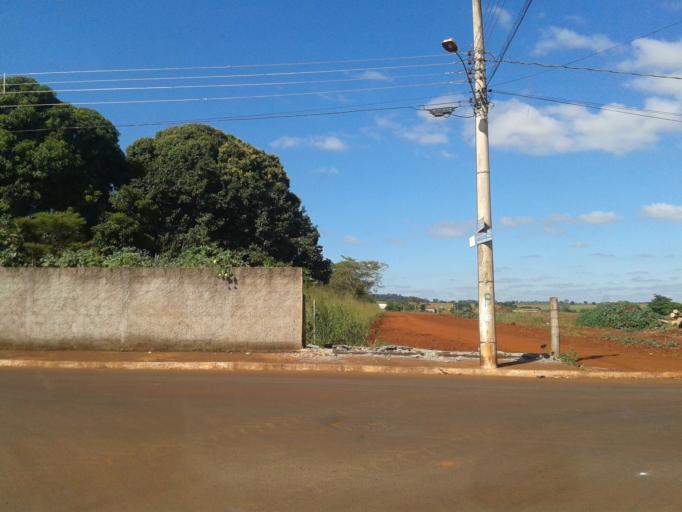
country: BR
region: Minas Gerais
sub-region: Centralina
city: Centralina
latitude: -18.5892
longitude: -49.2029
